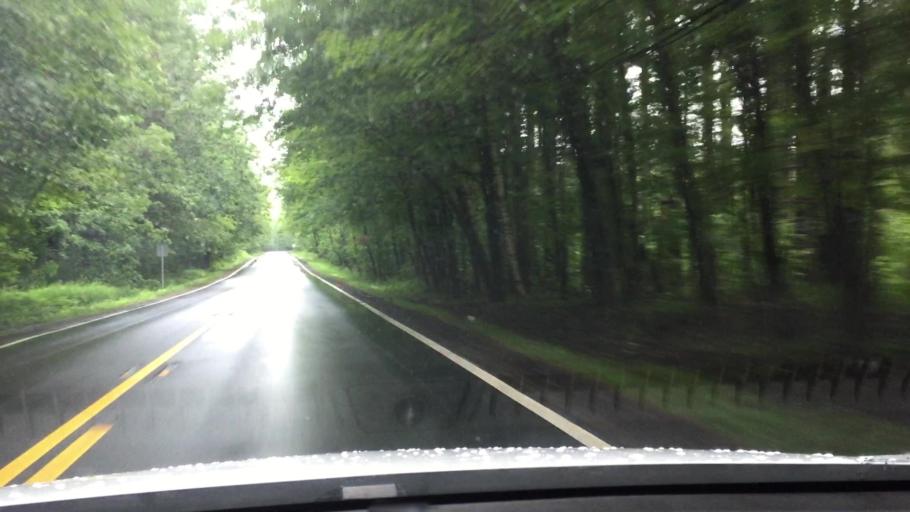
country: US
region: Massachusetts
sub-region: Berkshire County
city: Hinsdale
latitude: 42.3996
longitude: -73.1706
